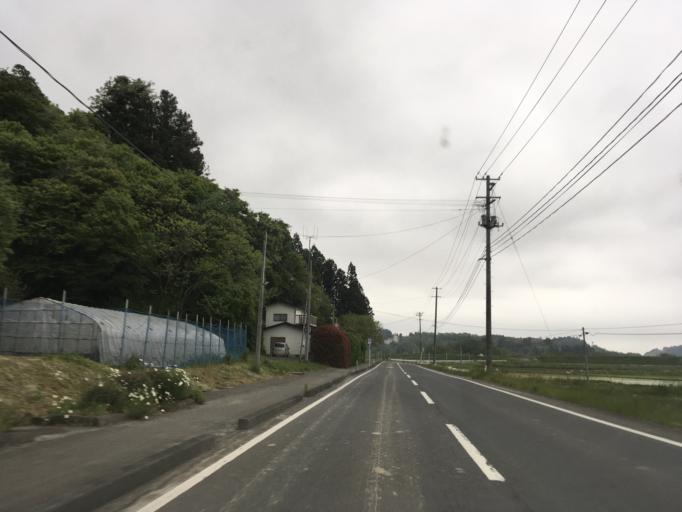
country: JP
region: Miyagi
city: Wakuya
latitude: 38.7227
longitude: 141.2958
